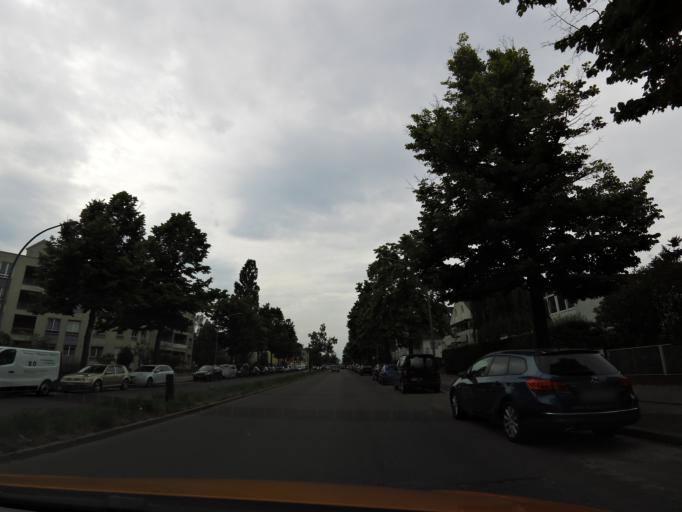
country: DE
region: Berlin
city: Lichterfelde
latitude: 52.4153
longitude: 13.3170
